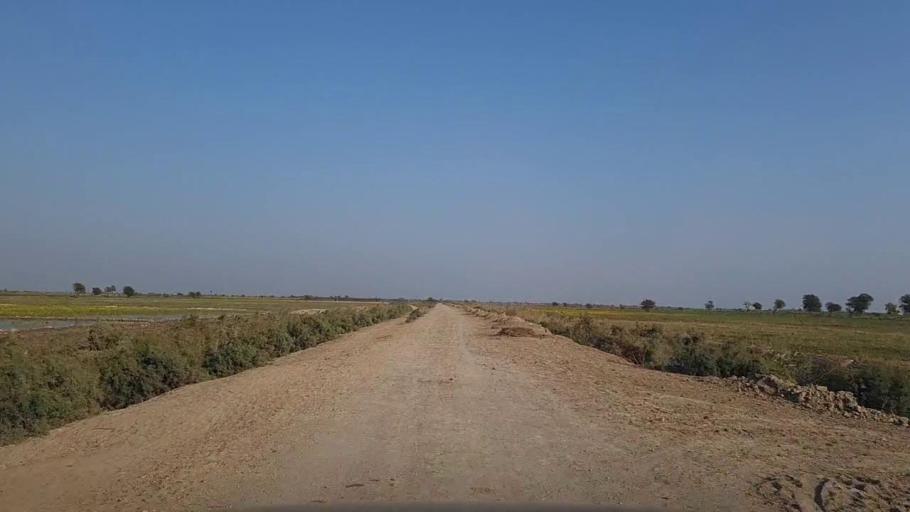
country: PK
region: Sindh
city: Tando Mittha Khan
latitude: 25.9252
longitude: 69.0770
